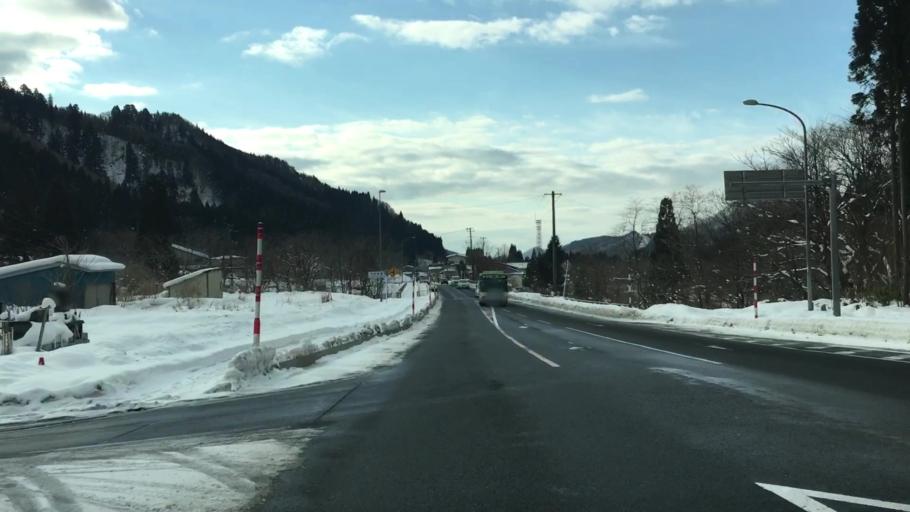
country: JP
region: Akita
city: Odate
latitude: 40.4027
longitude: 140.6071
